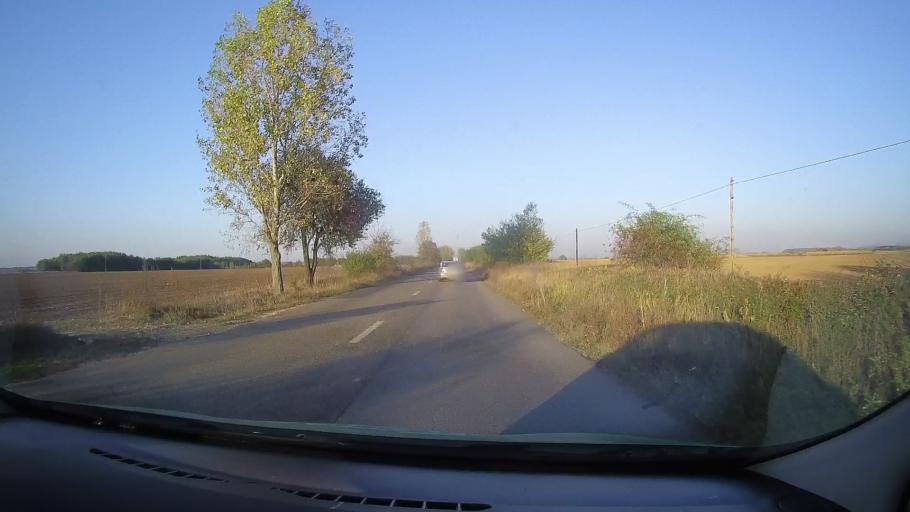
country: RO
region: Bihor
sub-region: Comuna Salard
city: Salard
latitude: 47.2047
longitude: 22.0138
